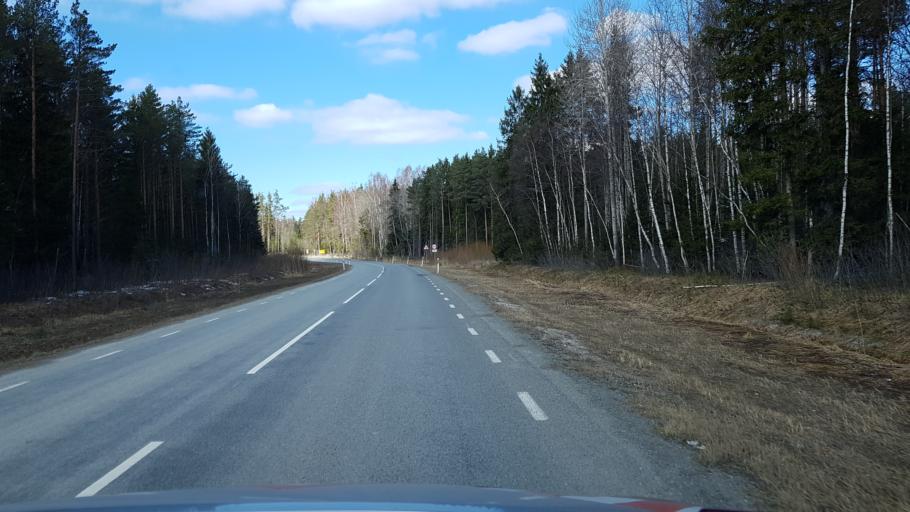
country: EE
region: Laeaene-Virumaa
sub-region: Tapa vald
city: Tapa
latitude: 59.2755
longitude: 25.9143
